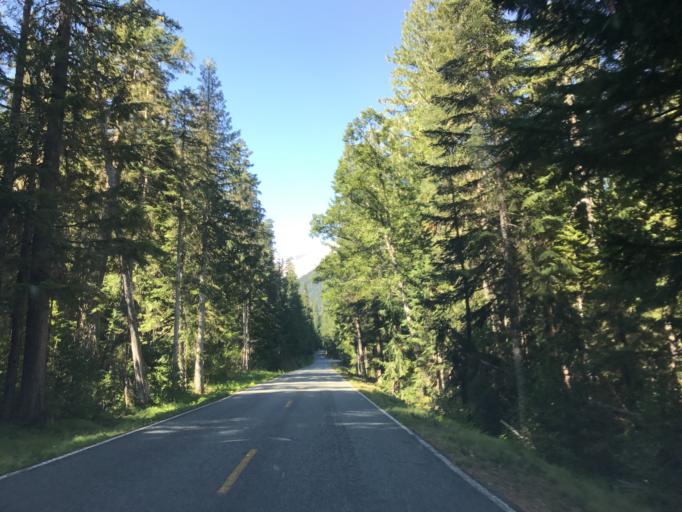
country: US
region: Washington
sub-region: King County
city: Enumclaw
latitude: 46.8933
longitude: -121.5898
